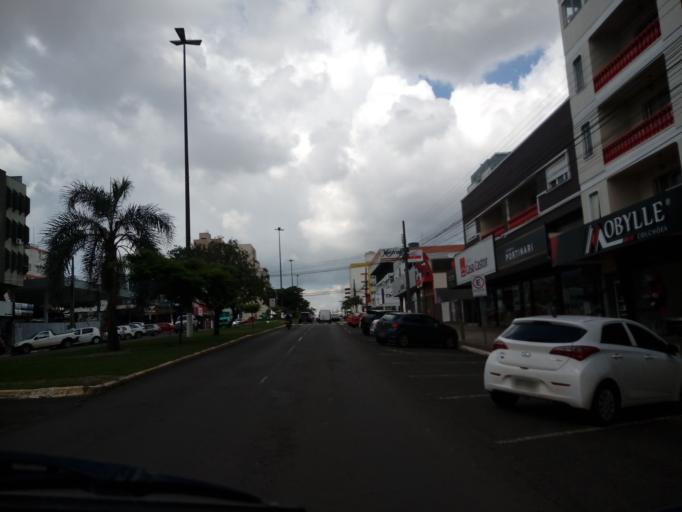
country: BR
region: Santa Catarina
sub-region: Chapeco
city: Chapeco
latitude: -27.0945
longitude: -52.6172
